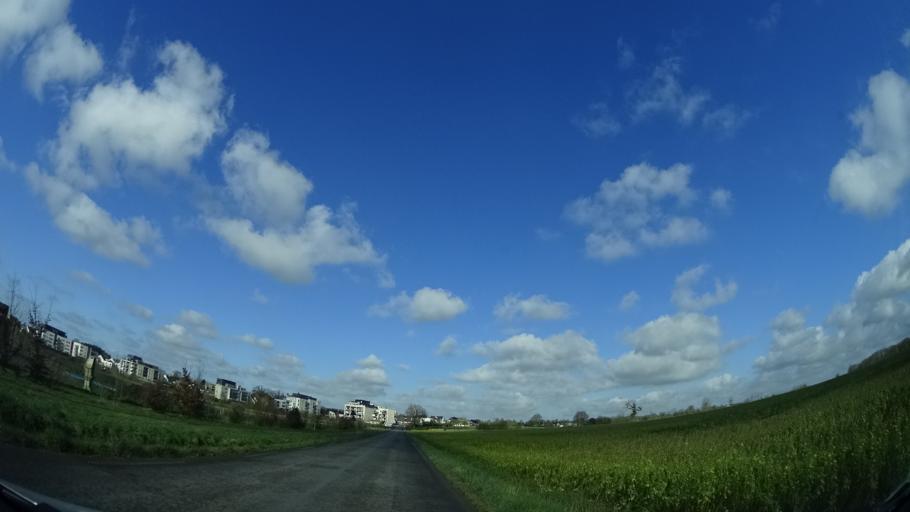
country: FR
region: Brittany
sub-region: Departement d'Ille-et-Vilaine
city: Pace
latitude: 48.1581
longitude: -1.7599
